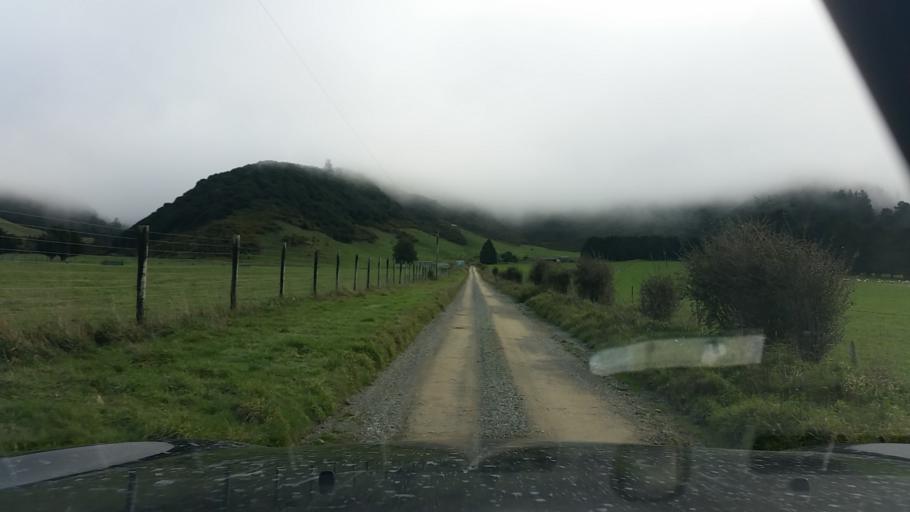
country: NZ
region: Marlborough
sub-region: Marlborough District
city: Picton
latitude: -41.1721
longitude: 173.9662
